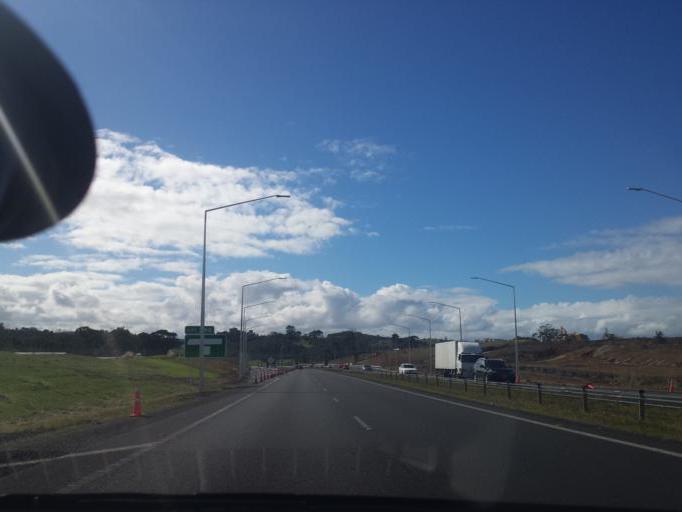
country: NZ
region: Auckland
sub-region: Auckland
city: Rothesay Bay
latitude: -36.6068
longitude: 174.6608
